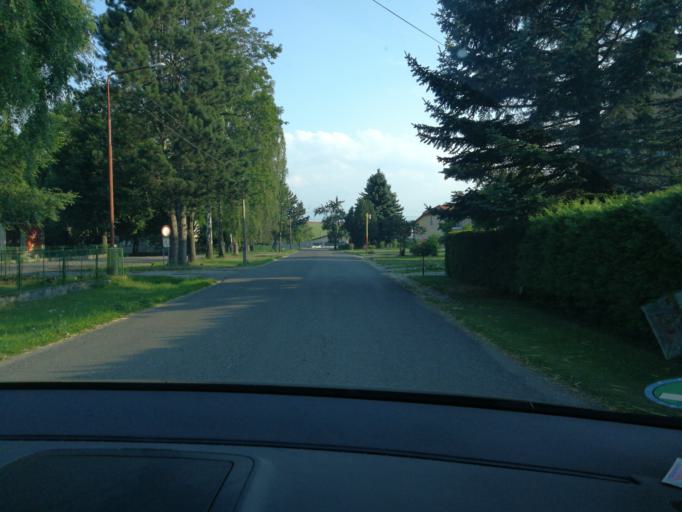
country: SK
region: Zilinsky
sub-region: Okres Liptovsky Mikulas
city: Liptovsky Mikulas
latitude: 49.1631
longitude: 19.5396
